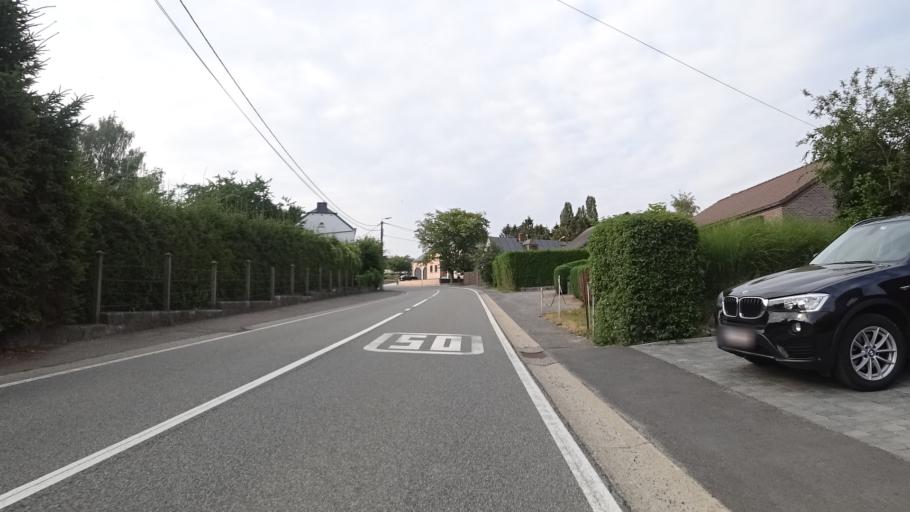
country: BE
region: Wallonia
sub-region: Province de Namur
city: Namur
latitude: 50.5162
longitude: 4.8440
